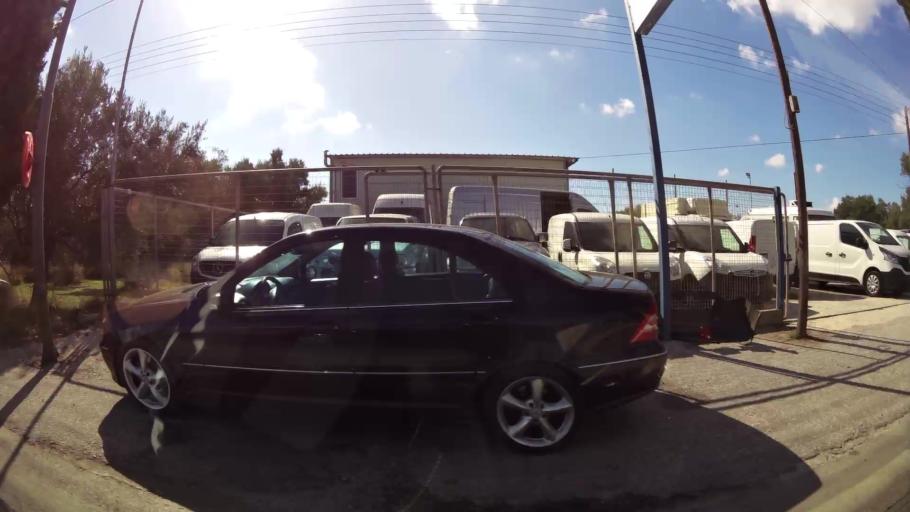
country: GR
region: Attica
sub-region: Nomarchia Anatolikis Attikis
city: Koropi
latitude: 37.8879
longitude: 23.8970
